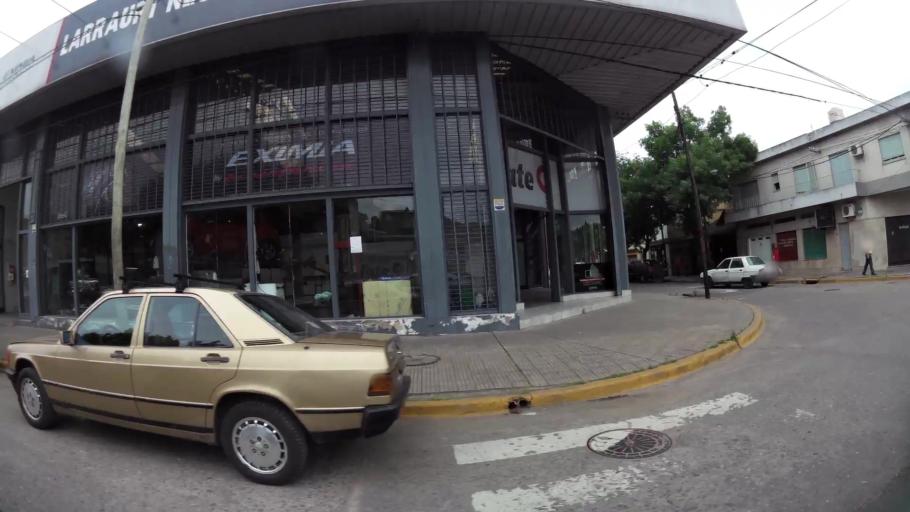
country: AR
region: Santa Fe
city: Gobernador Galvez
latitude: -33.0031
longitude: -60.6506
